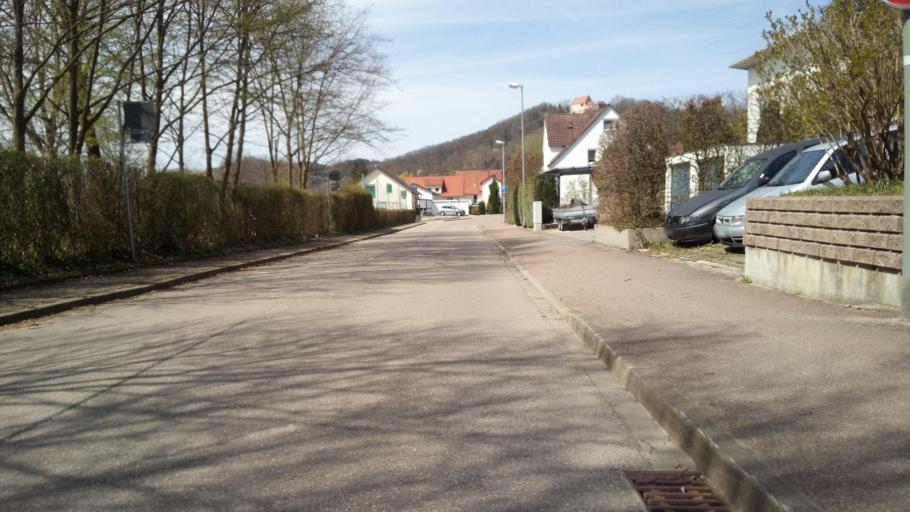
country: DE
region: Baden-Wuerttemberg
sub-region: Regierungsbezirk Stuttgart
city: Donzdorf
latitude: 48.6884
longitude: 9.7988
